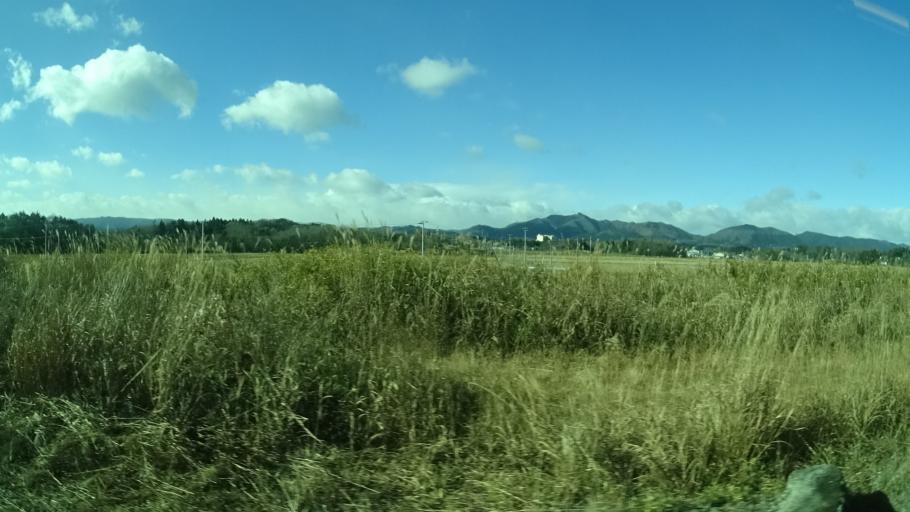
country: JP
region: Miyagi
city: Marumori
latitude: 37.8572
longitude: 140.9300
